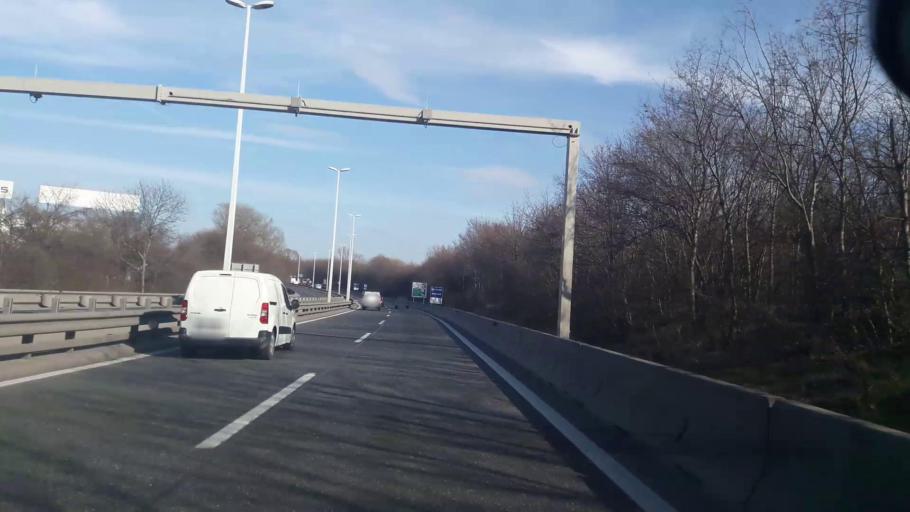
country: AT
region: Lower Austria
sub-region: Politischer Bezirk Korneuburg
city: Langenzersdorf
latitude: 48.2812
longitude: 16.3710
